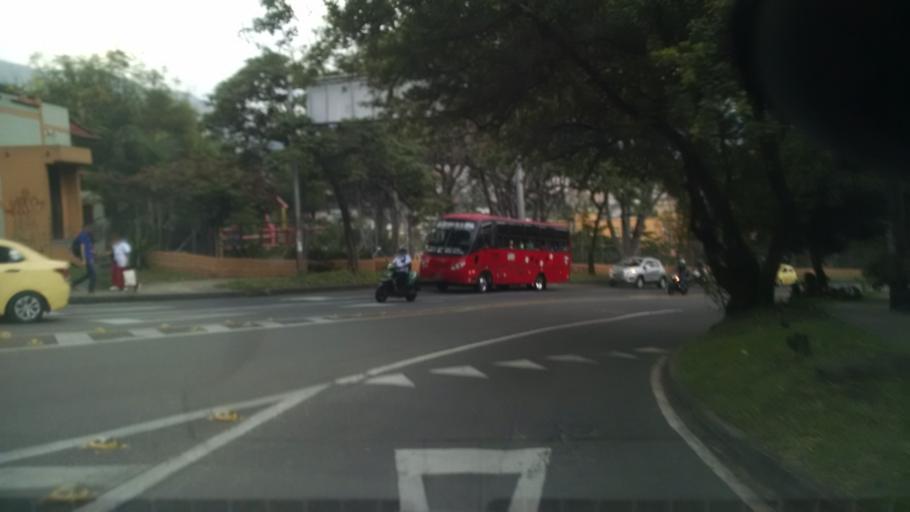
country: CO
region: Antioquia
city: Medellin
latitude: 6.2759
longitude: -75.5789
